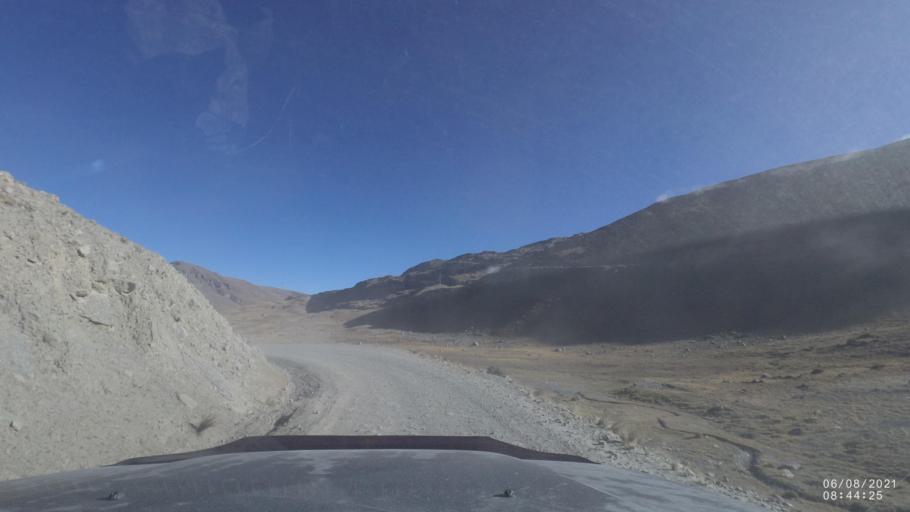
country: BO
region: Cochabamba
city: Sipe Sipe
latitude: -17.1714
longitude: -66.4103
